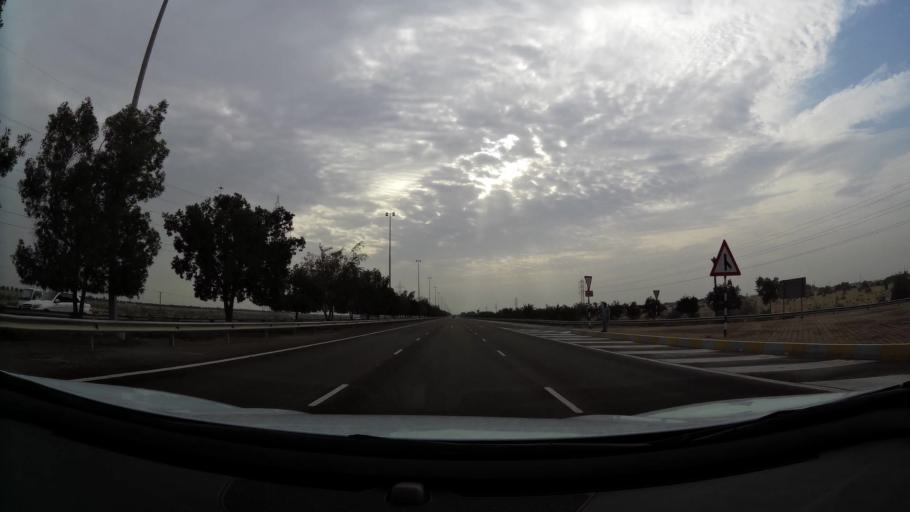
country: AE
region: Abu Dhabi
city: Abu Dhabi
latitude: 24.2019
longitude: 54.9079
